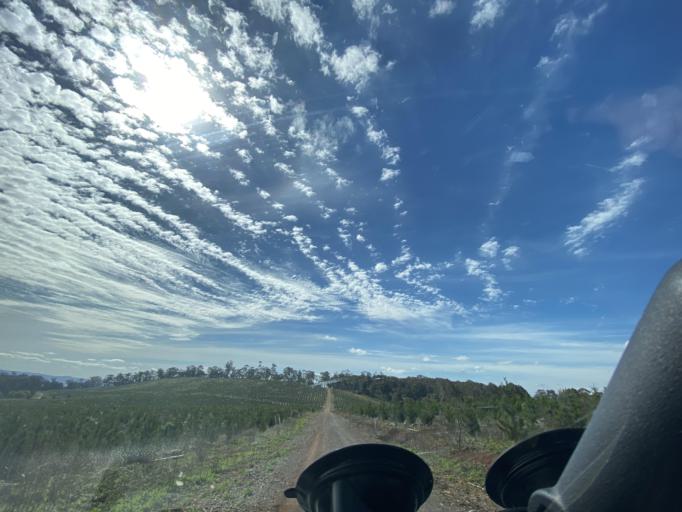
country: AU
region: Victoria
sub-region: Mansfield
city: Mansfield
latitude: -36.8224
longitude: 146.1032
